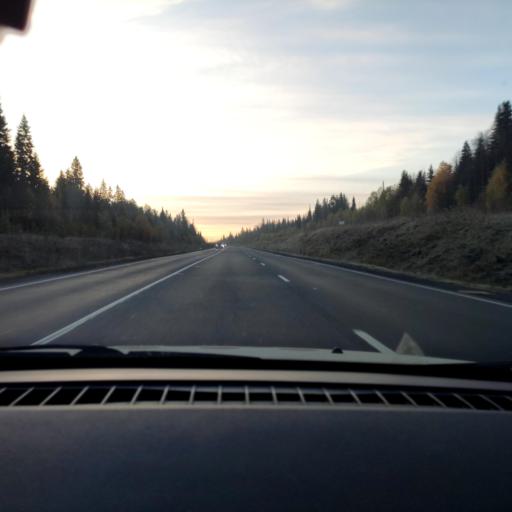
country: RU
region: Perm
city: Novyye Lyady
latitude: 58.0364
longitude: 56.4721
